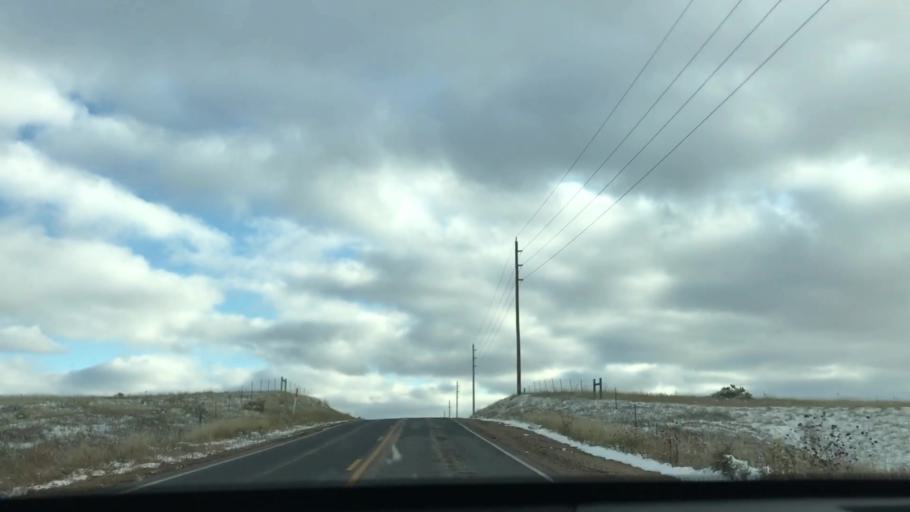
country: US
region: Colorado
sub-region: Boulder County
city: Lafayette
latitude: 39.9620
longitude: -105.0719
